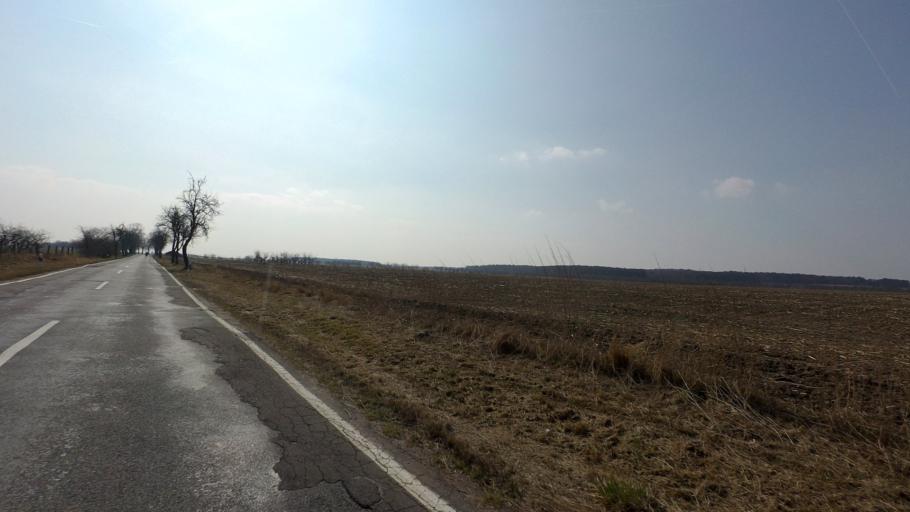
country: DE
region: Brandenburg
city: Gross Kreutz
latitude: 52.4313
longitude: 12.7864
